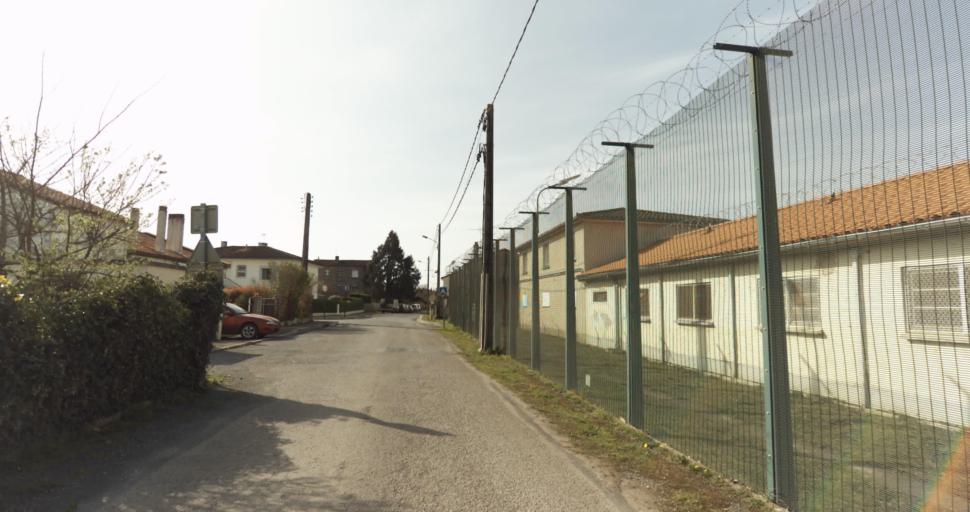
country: FR
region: Midi-Pyrenees
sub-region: Departement du Tarn
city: Saint-Sulpice-la-Pointe
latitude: 43.7748
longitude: 1.6899
